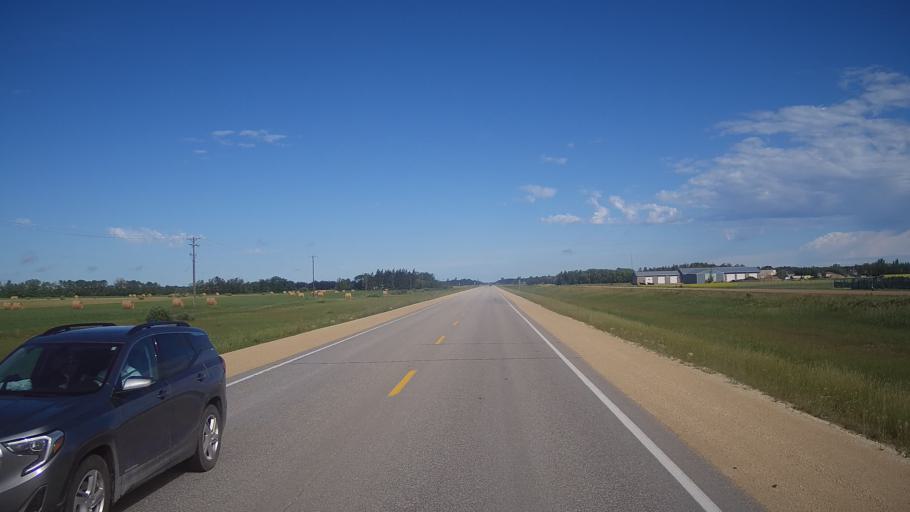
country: CA
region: Manitoba
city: Stonewall
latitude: 50.1977
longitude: -97.6477
